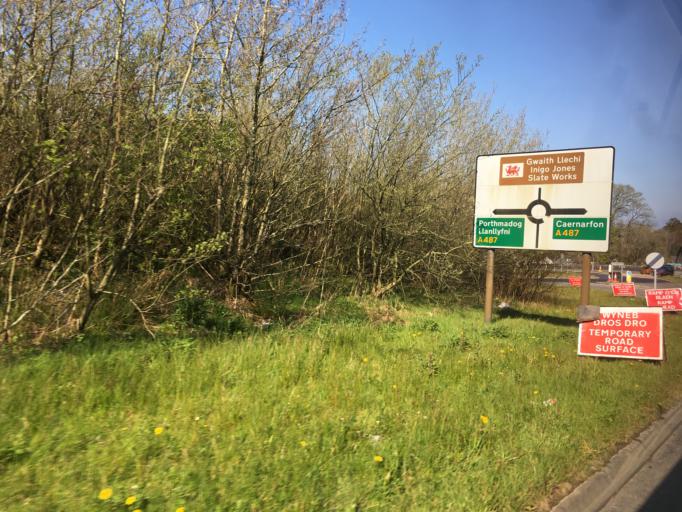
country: GB
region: Wales
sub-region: Gwynedd
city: Llanwnda
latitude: 53.0697
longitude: -4.2829
